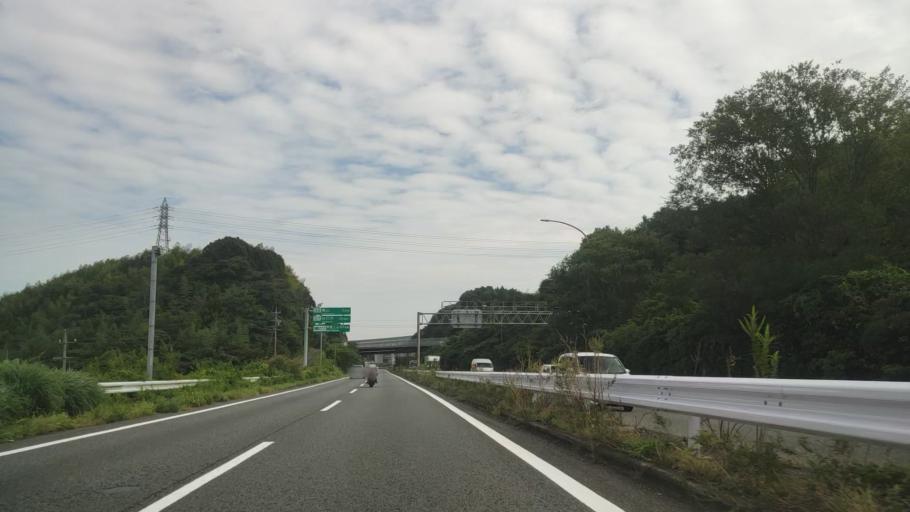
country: JP
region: Mie
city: Kameyama
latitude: 34.8462
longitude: 136.4114
